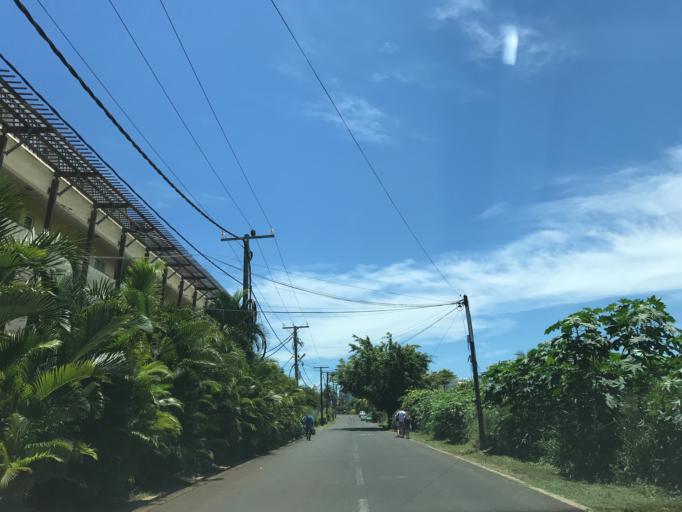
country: MU
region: Black River
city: Flic en Flac
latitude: -20.2827
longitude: 57.3681
